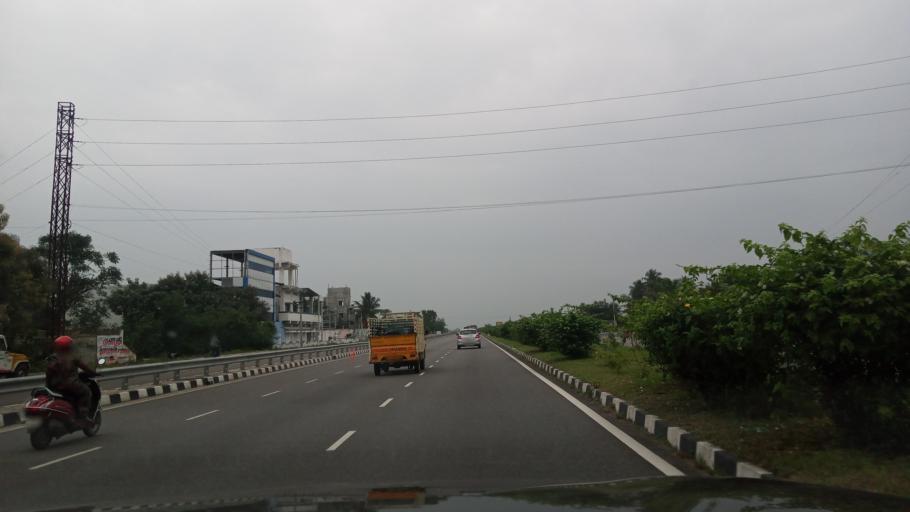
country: IN
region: Tamil Nadu
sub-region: Vellore
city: Pallikondai
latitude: 12.9119
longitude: 79.0011
